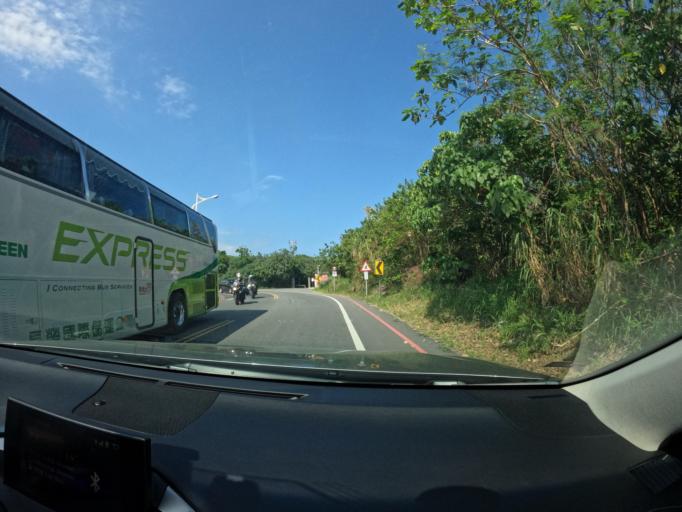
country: TW
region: Taiwan
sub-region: Hualien
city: Hualian
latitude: 24.0165
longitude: 121.6382
